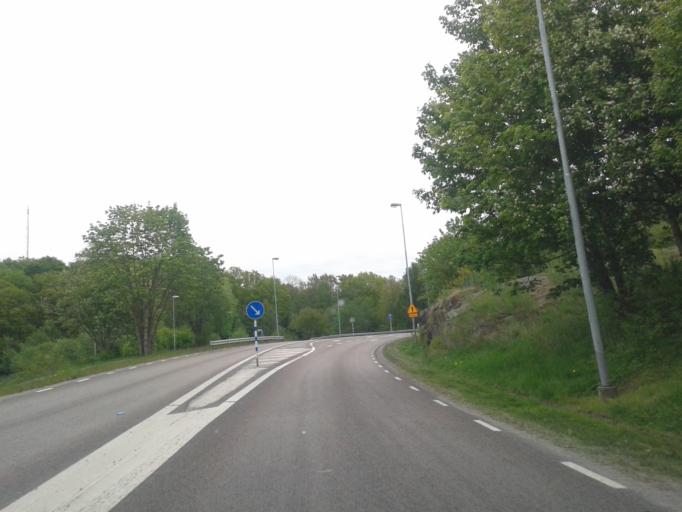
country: SE
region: Vaestra Goetaland
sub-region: Kungalvs Kommun
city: Kungalv
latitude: 57.8860
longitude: 11.9683
